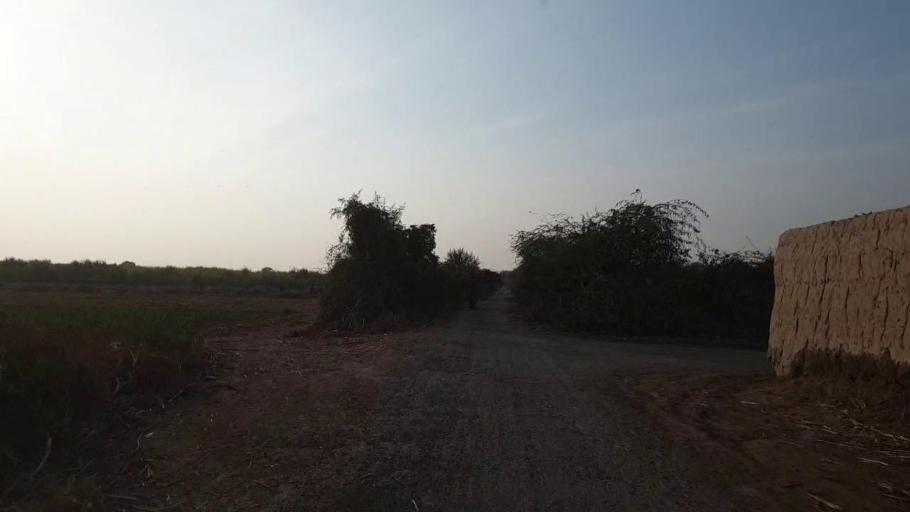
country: PK
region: Sindh
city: Matiari
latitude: 25.5997
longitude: 68.4353
